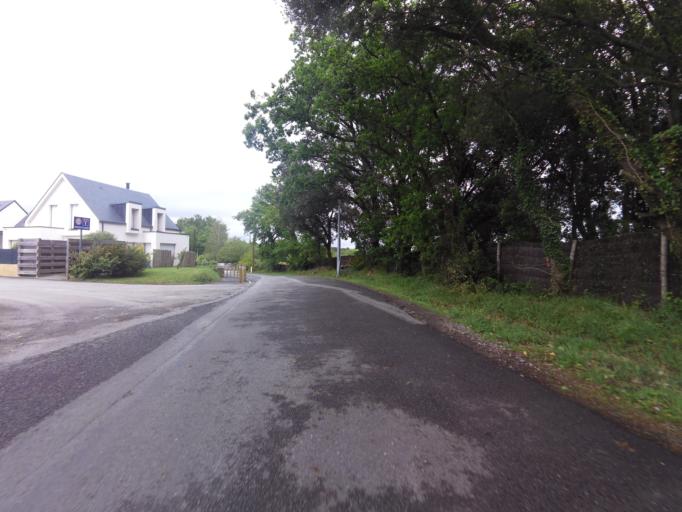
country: FR
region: Brittany
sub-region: Departement du Morbihan
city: Baden
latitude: 47.6110
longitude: -2.9204
